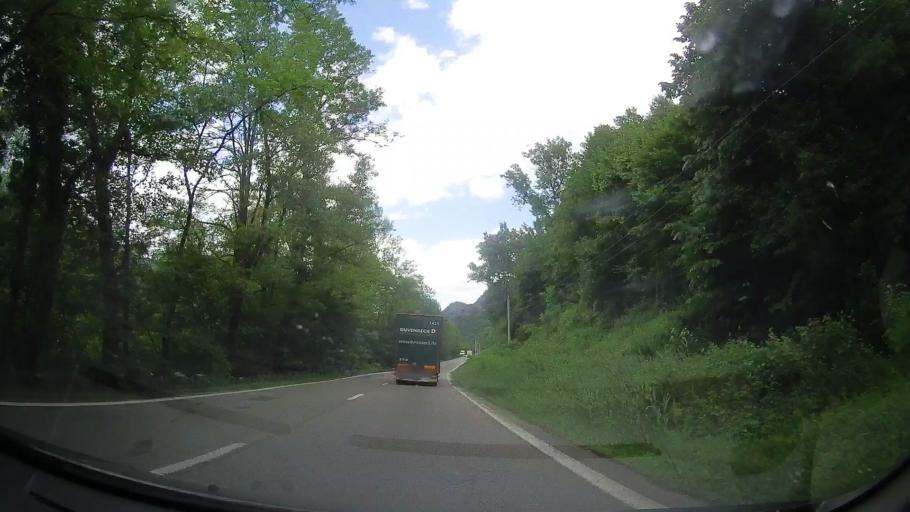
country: RO
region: Valcea
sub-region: Oras Calimanesti
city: Calimanesti
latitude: 45.2734
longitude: 24.3172
